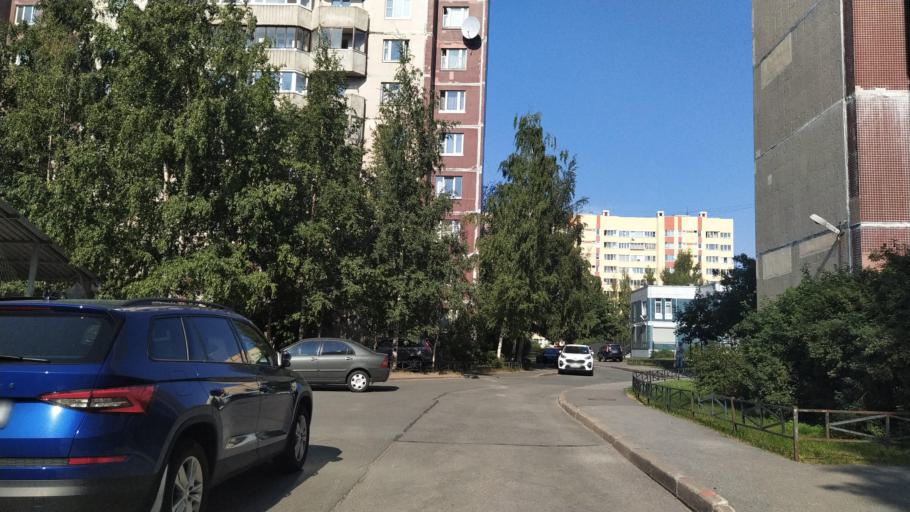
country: RU
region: Leningrad
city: Untolovo
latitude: 59.9899
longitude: 30.2135
